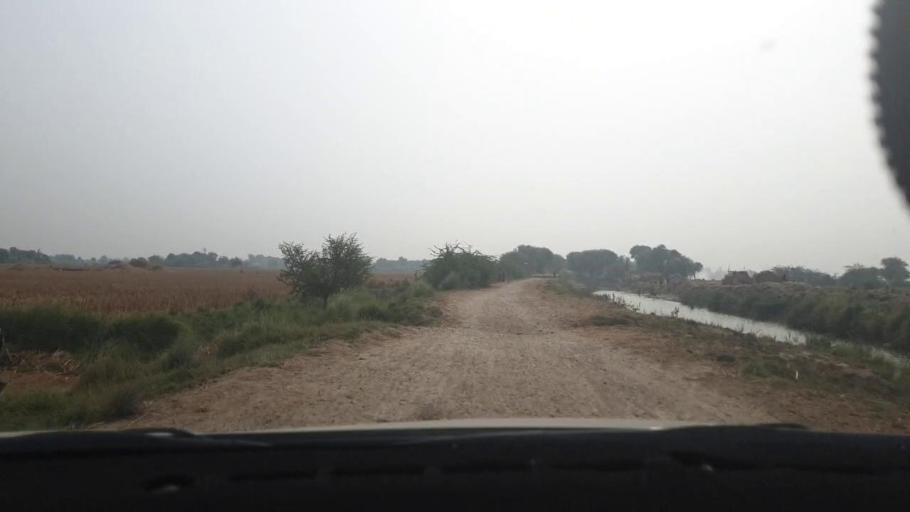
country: PK
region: Sindh
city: Tando Muhammad Khan
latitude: 25.0652
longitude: 68.5070
